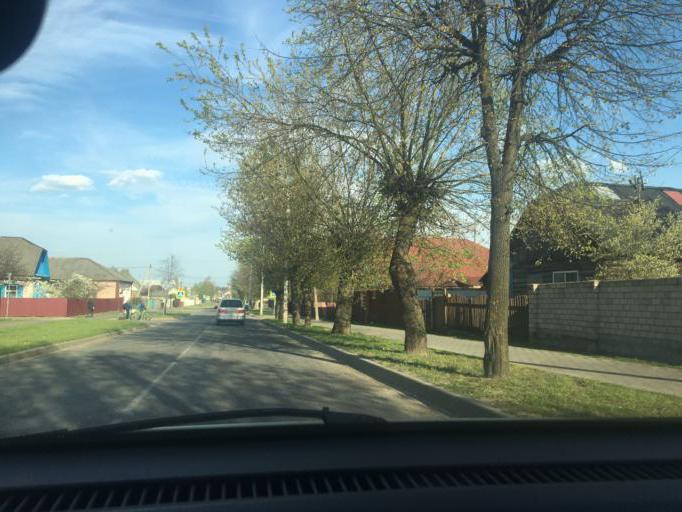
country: BY
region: Mogilev
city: Babruysk
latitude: 53.1474
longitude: 29.1976
